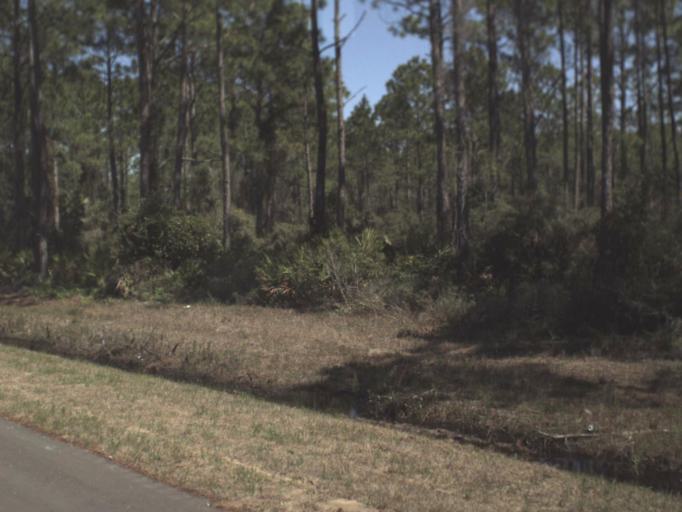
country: US
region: Florida
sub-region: Gulf County
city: Port Saint Joe
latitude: 29.7067
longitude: -85.3042
